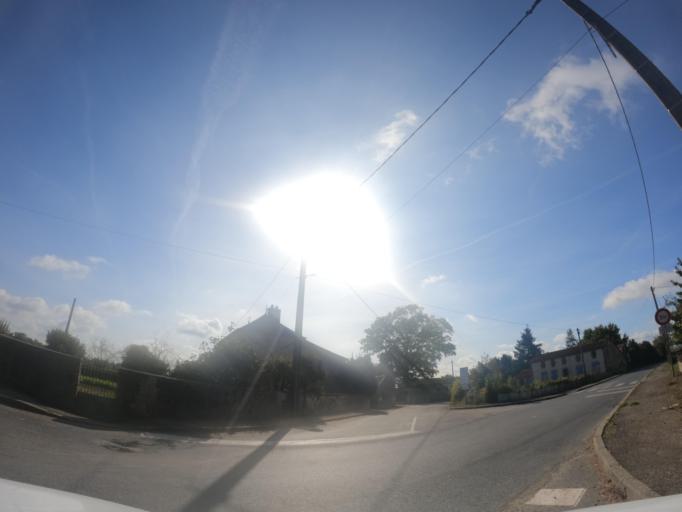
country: FR
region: Poitou-Charentes
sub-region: Departement des Deux-Sevres
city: Courlay
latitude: 46.7799
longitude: -0.5759
